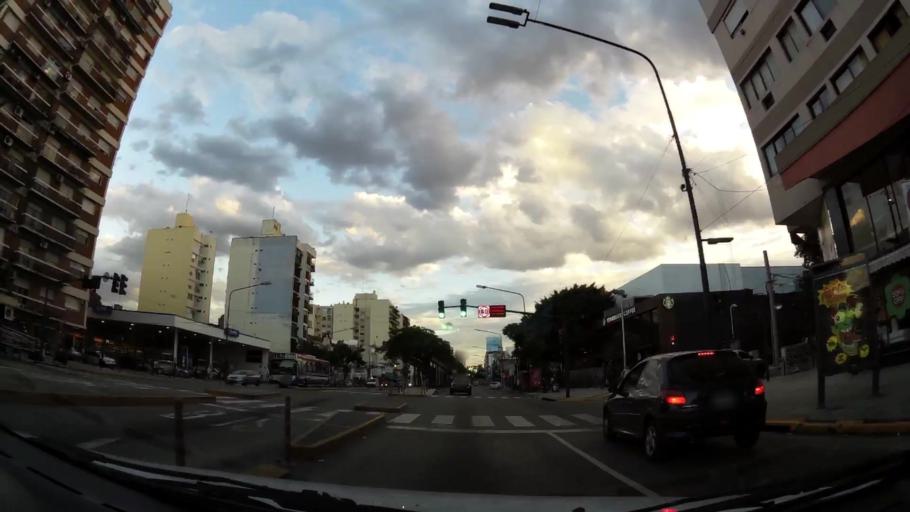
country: AR
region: Buenos Aires
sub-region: Partido de Vicente Lopez
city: Olivos
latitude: -34.5288
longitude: -58.4812
